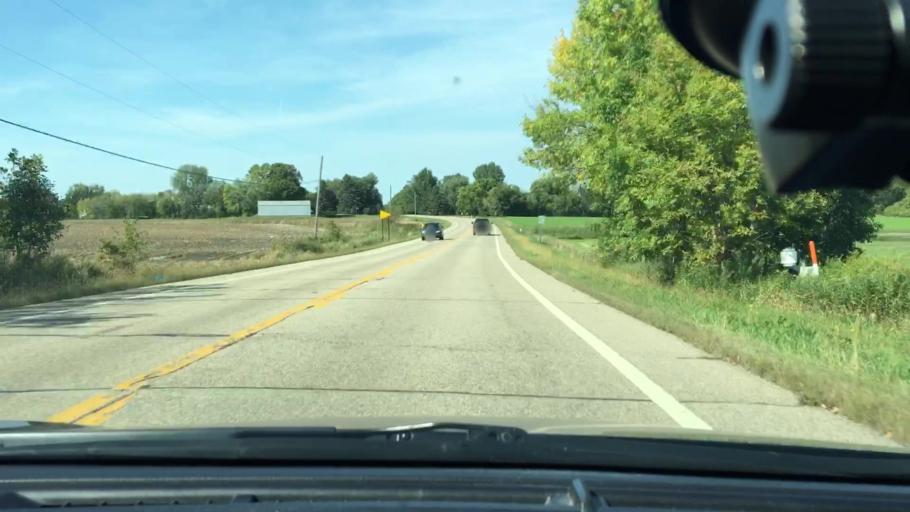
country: US
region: Minnesota
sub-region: Wright County
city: Hanover
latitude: 45.1217
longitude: -93.6104
